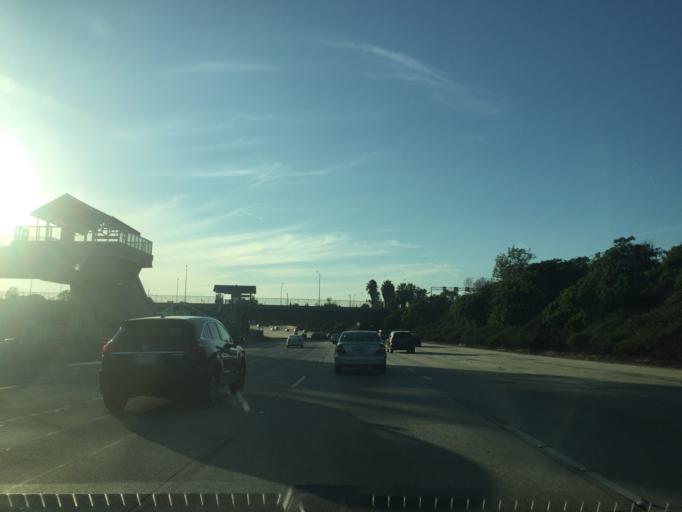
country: US
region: California
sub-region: Los Angeles County
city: Lennox
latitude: 33.9334
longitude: -118.3506
